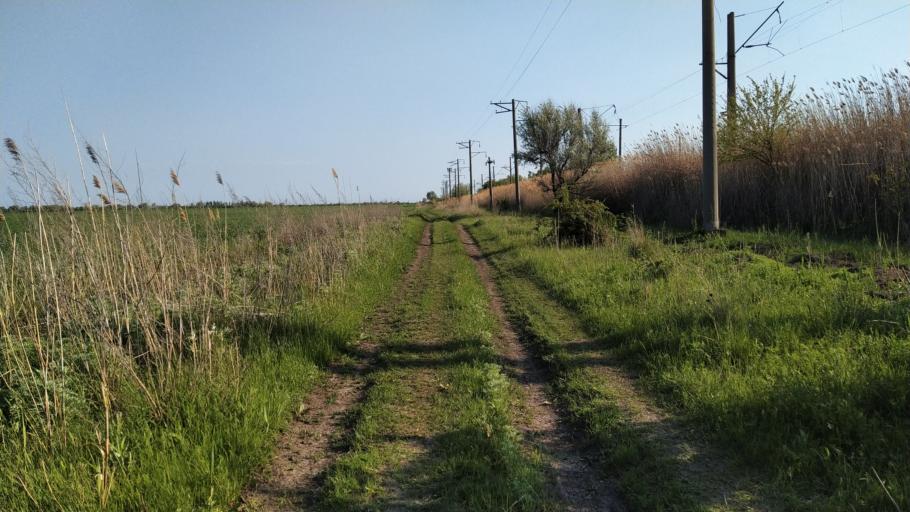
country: RU
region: Rostov
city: Bataysk
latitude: 47.1168
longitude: 39.7138
